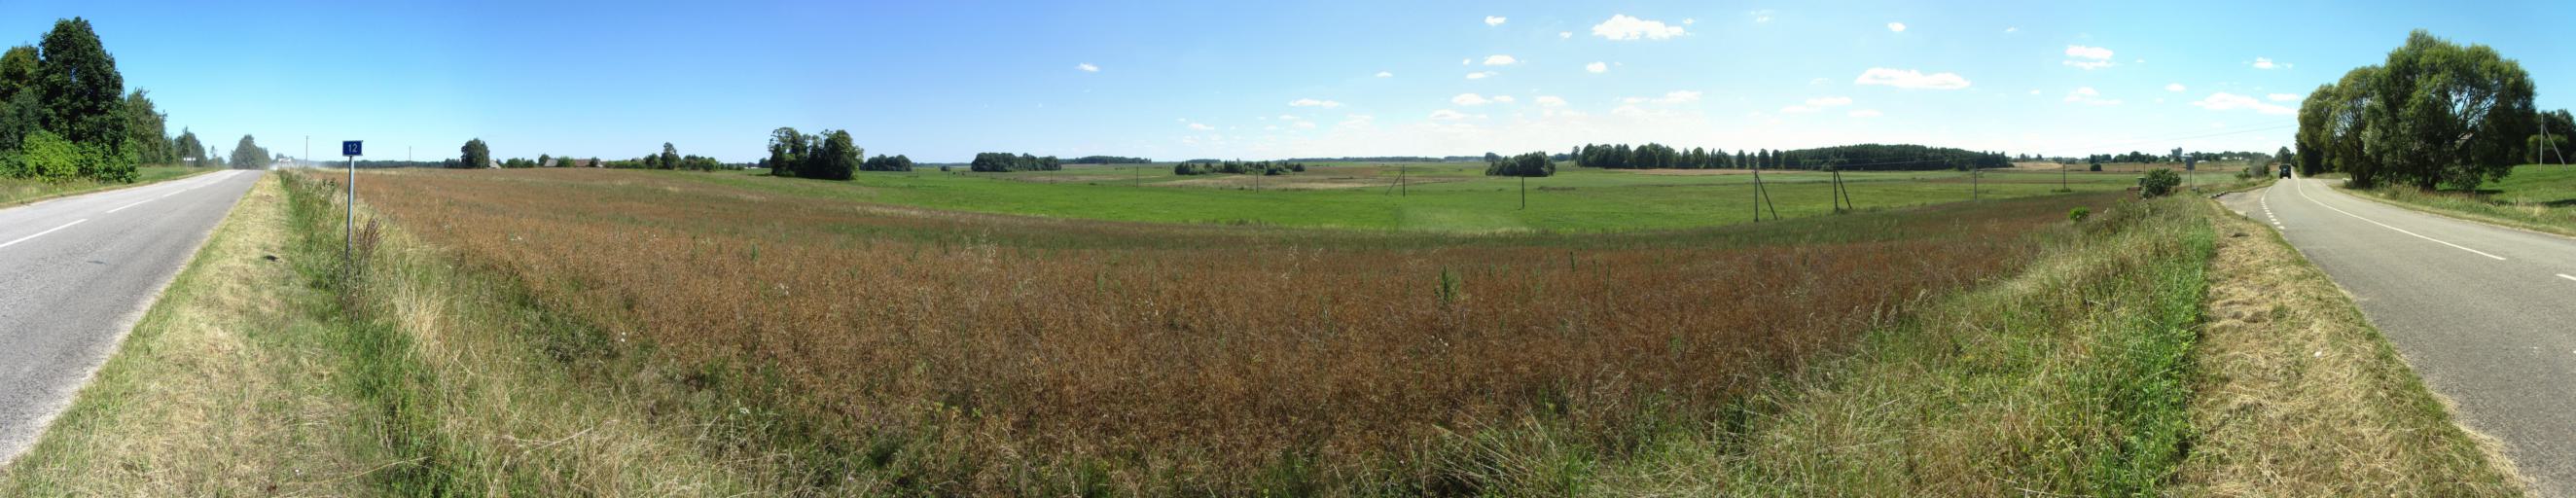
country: LT
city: Obeliai
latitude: 55.8455
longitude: 25.1502
